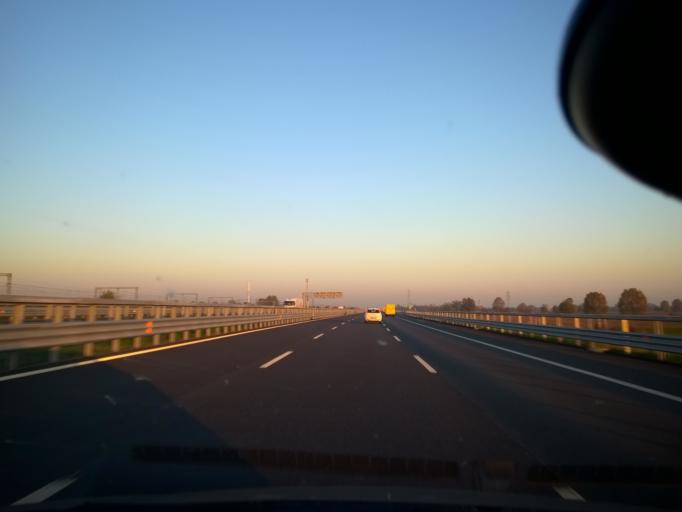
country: IT
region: Lombardy
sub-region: Citta metropolitana di Milano
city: Pozzuolo Martesana
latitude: 45.5073
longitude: 9.4660
